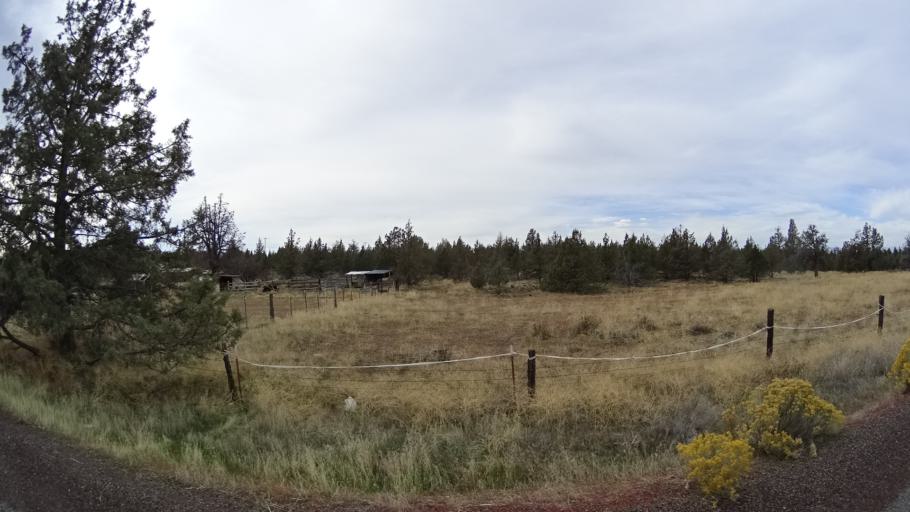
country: US
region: California
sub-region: Siskiyou County
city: Weed
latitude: 41.6106
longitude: -122.3668
